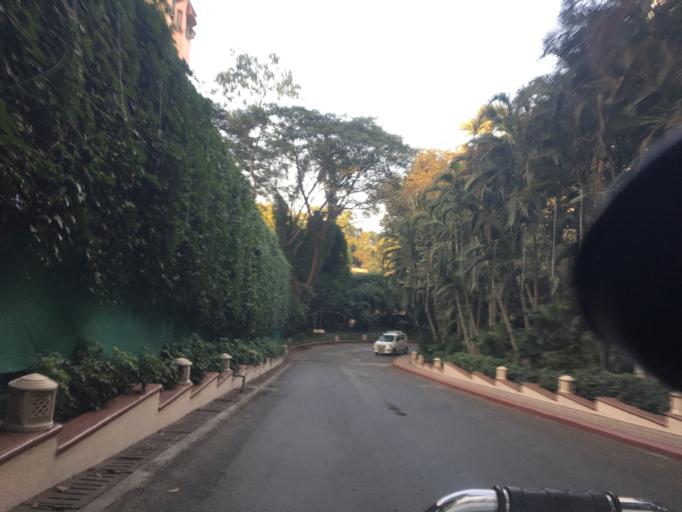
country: IN
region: Maharashtra
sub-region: Mumbai Suburban
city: Powai
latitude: 19.1325
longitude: 72.8987
